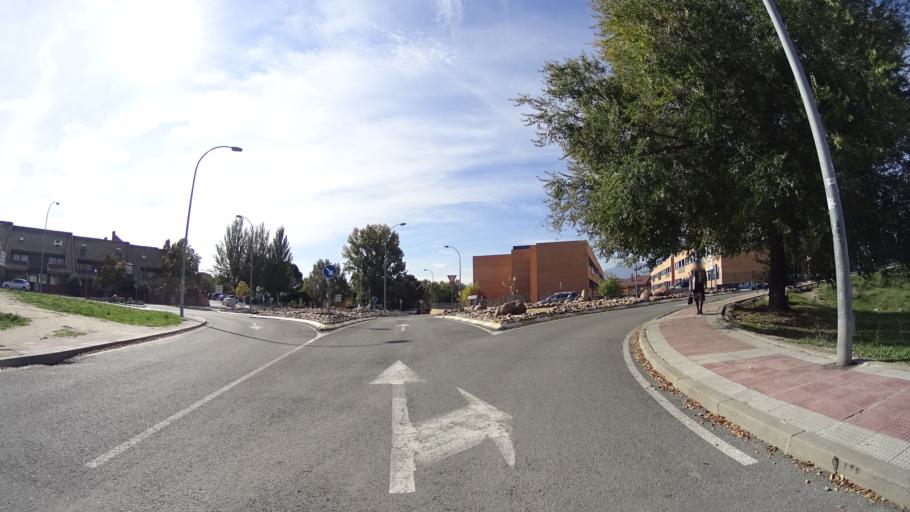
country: ES
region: Madrid
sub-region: Provincia de Madrid
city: Collado-Villalba
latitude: 40.6241
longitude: -4.0154
